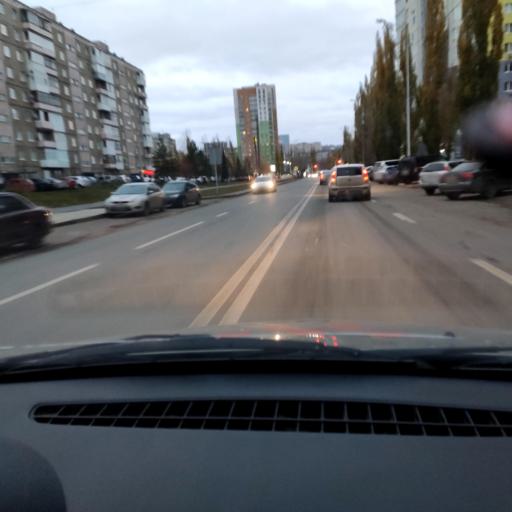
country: RU
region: Bashkortostan
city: Ufa
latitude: 54.7677
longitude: 56.0600
